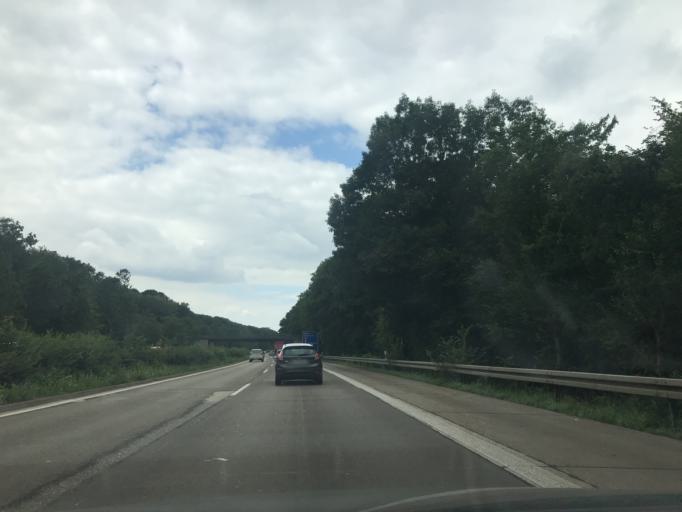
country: DE
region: North Rhine-Westphalia
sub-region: Regierungsbezirk Dusseldorf
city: Erkrath
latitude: 51.1803
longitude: 6.8814
